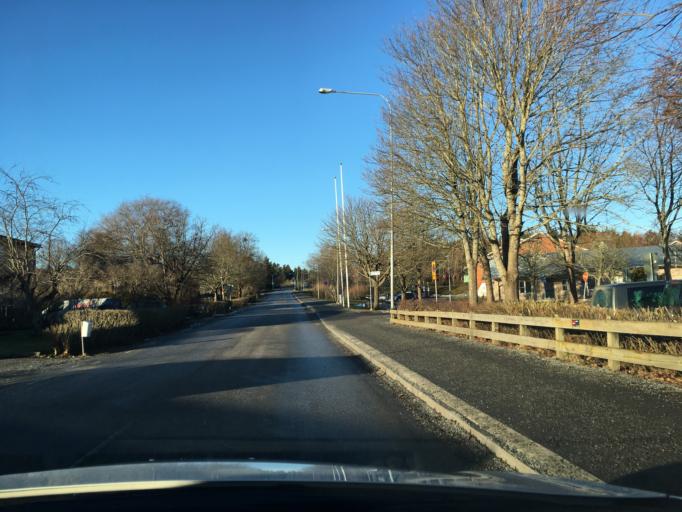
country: SE
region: Uppsala
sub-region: Knivsta Kommun
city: Knivsta
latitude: 59.7242
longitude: 17.7844
